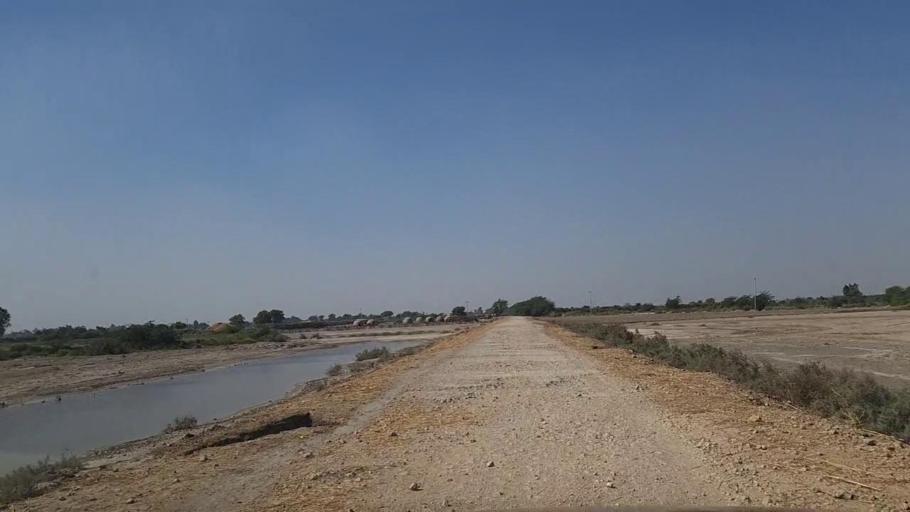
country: PK
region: Sindh
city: Daro Mehar
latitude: 24.8336
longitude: 68.1860
